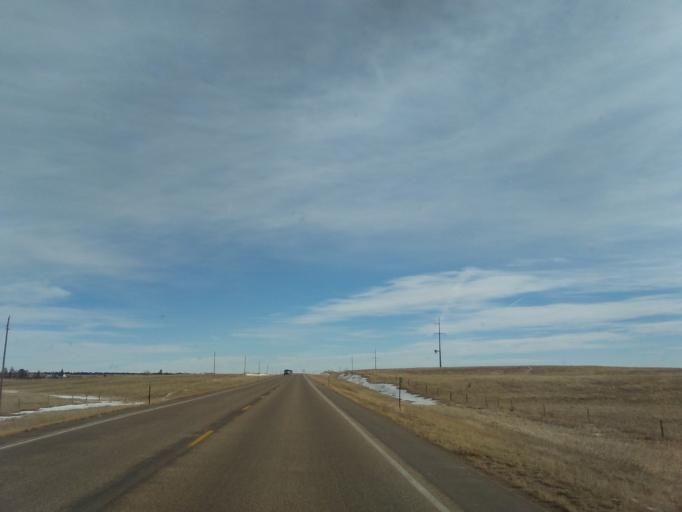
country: US
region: Wyoming
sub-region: Laramie County
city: Ranchettes
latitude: 41.4123
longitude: -104.4309
